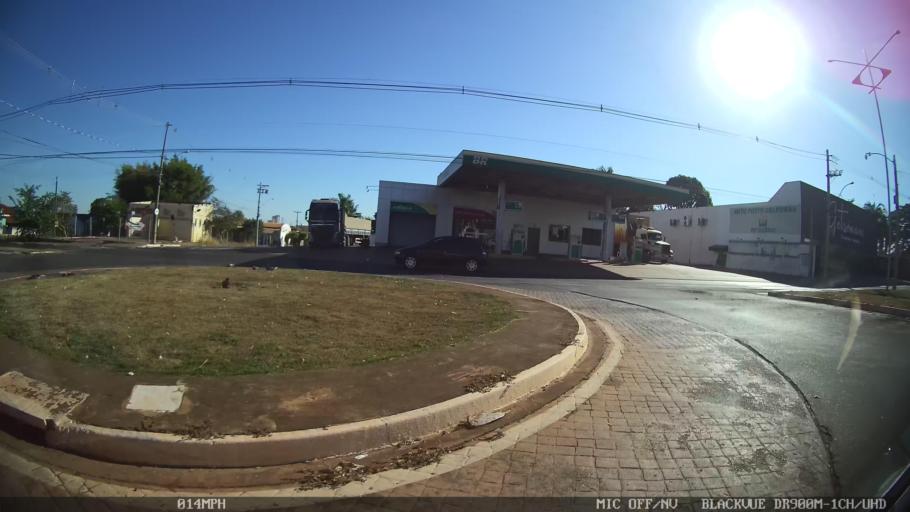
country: BR
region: Sao Paulo
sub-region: Olimpia
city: Olimpia
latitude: -20.7324
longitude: -48.9047
